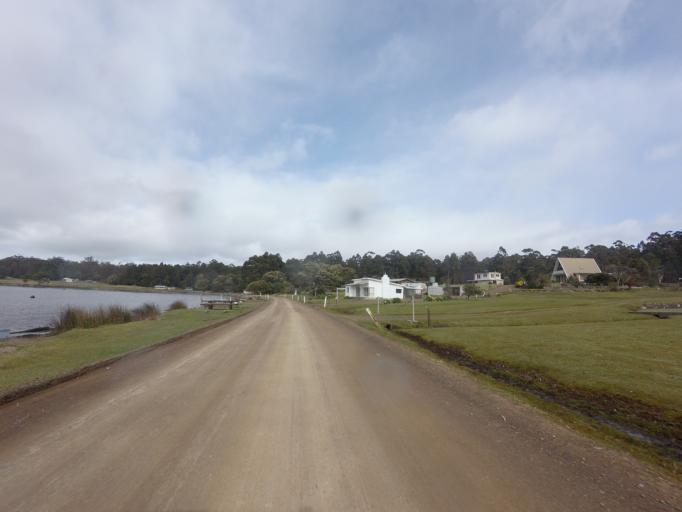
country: AU
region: Tasmania
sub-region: Huon Valley
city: Geeveston
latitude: -43.5333
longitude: 146.8918
